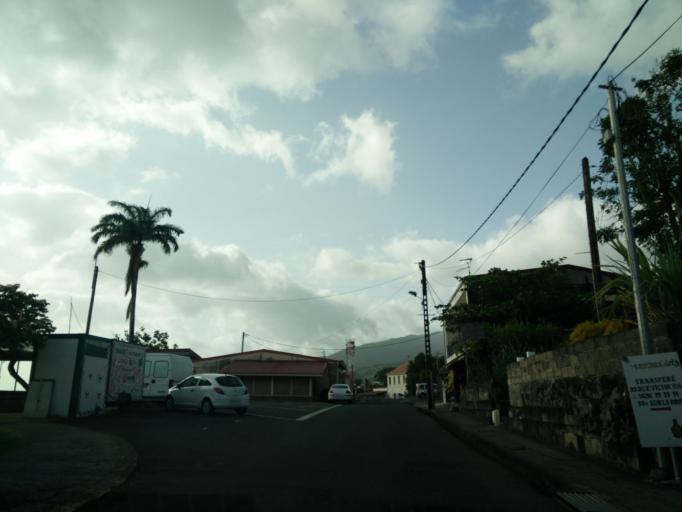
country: MQ
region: Martinique
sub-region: Martinique
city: Saint-Pierre
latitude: 14.7458
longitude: -61.1762
